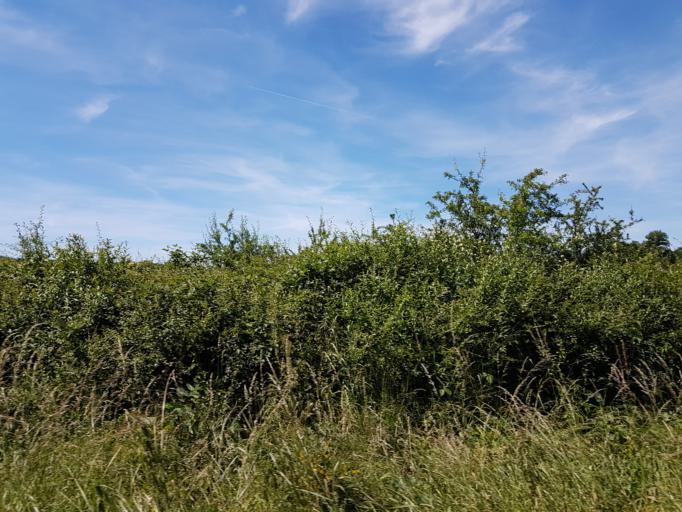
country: FR
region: Bourgogne
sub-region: Departement de Saone-et-Loire
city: Epinac
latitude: 47.0003
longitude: 4.4778
